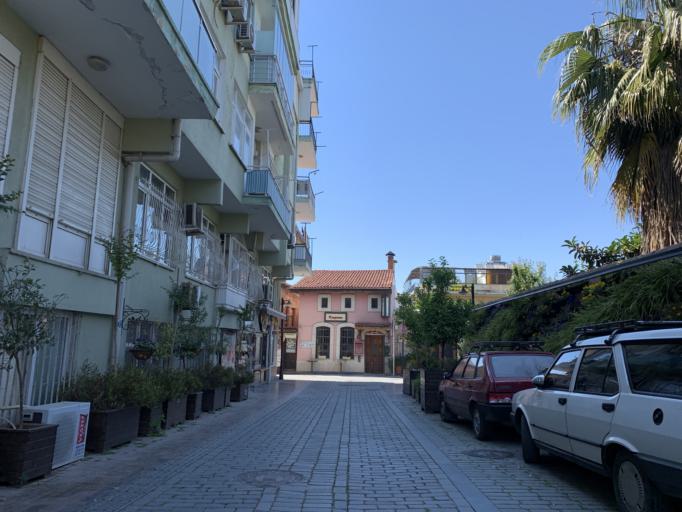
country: TR
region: Antalya
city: Antalya
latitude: 36.8831
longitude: 30.7054
